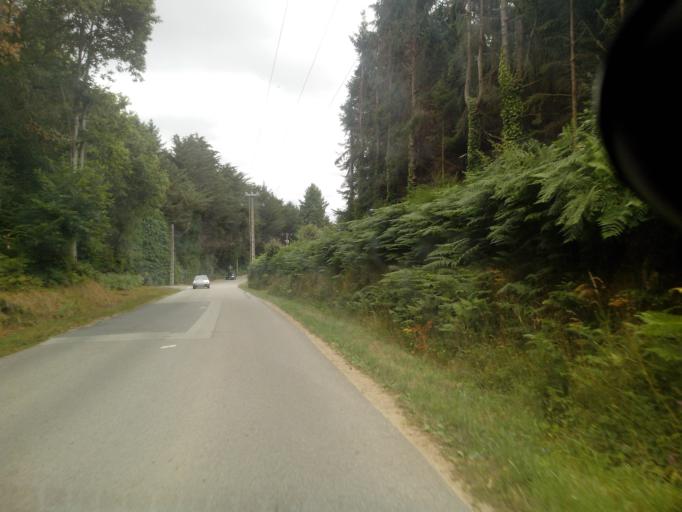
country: FR
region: Brittany
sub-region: Departement du Morbihan
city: Kervignac
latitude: 47.7566
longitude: -3.2702
